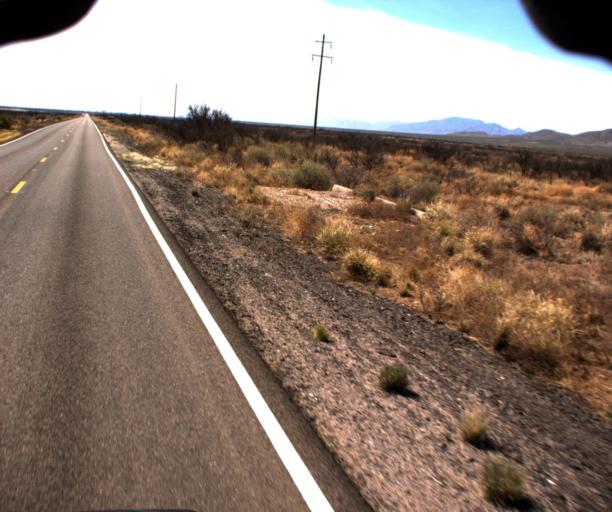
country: US
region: Arizona
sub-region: Cochise County
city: Willcox
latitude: 32.1669
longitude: -109.9447
